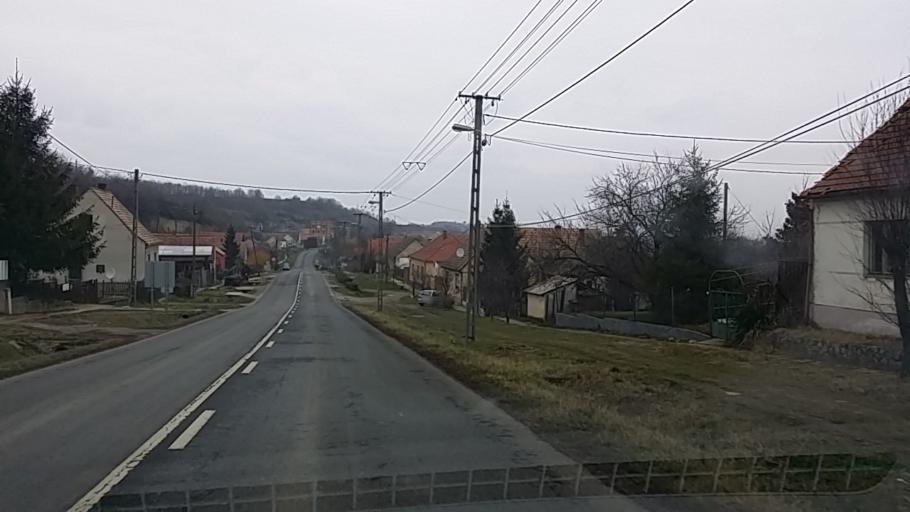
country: HU
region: Baranya
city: Dunaszekcso
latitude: 46.0727
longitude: 18.7536
